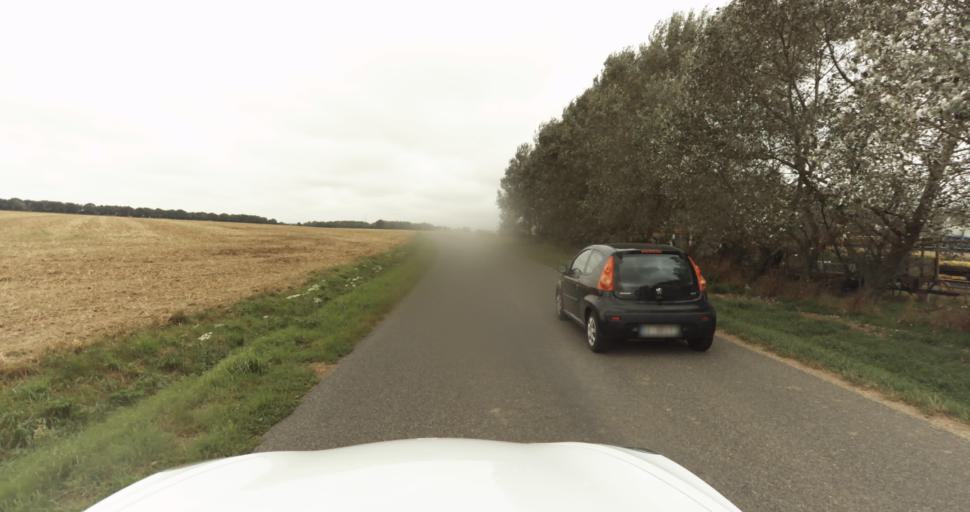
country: FR
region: Haute-Normandie
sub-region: Departement de l'Eure
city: Aviron
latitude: 49.0578
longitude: 1.0839
